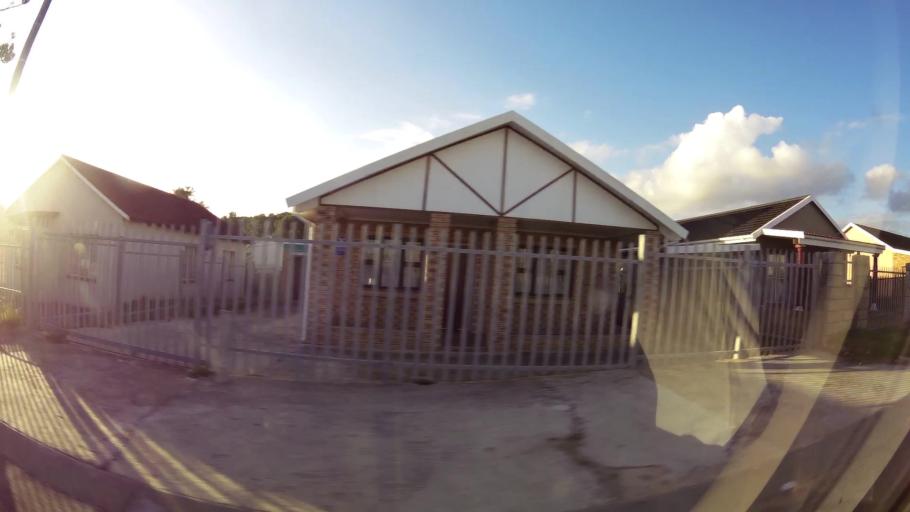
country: ZA
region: Western Cape
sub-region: Eden District Municipality
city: George
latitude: -34.0025
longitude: 22.6559
